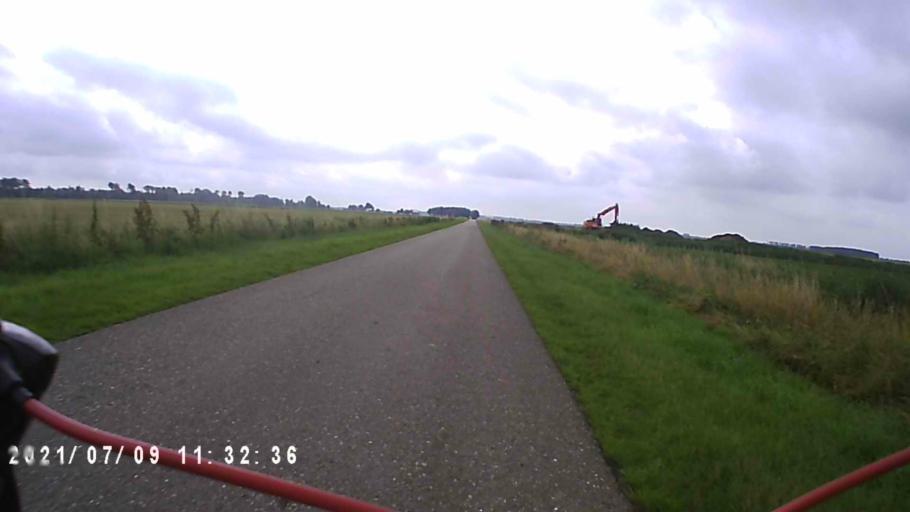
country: NL
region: Groningen
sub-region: Gemeente Slochteren
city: Slochteren
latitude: 53.2328
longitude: 6.8513
